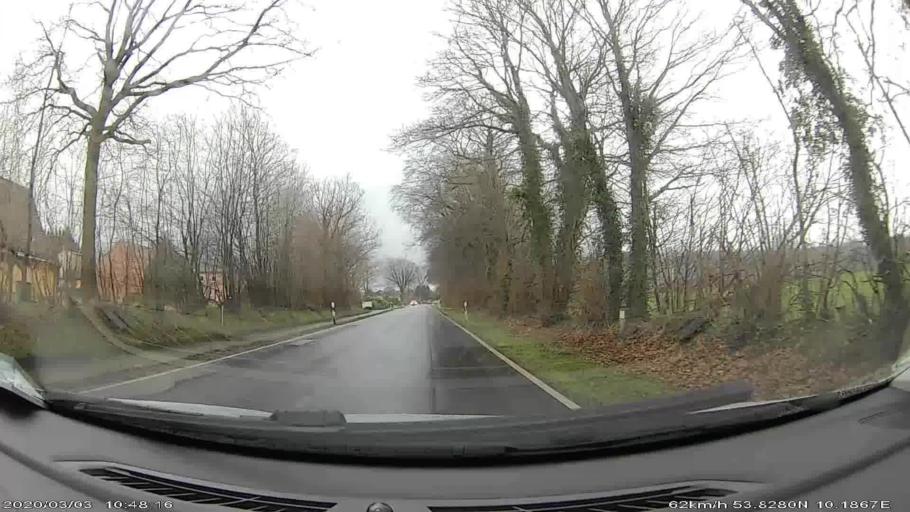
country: DE
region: Schleswig-Holstein
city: Itzstedt
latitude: 53.8251
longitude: 10.1866
